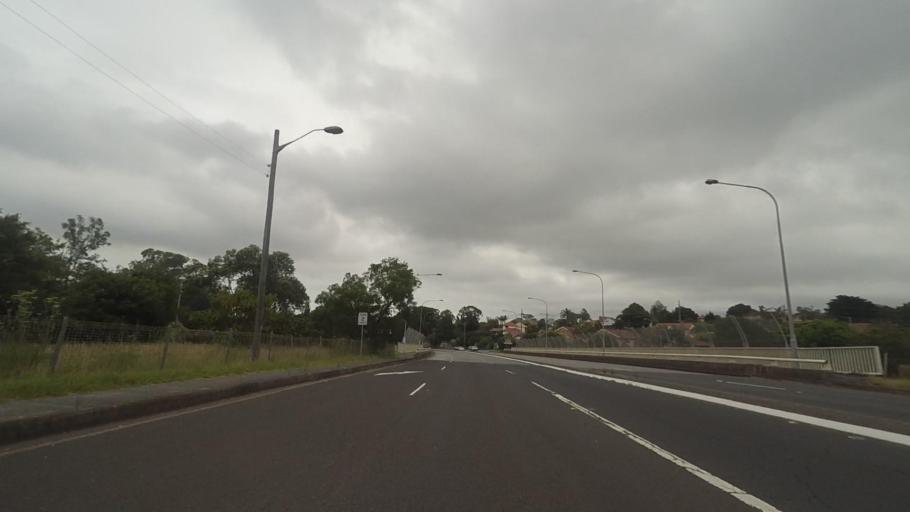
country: AU
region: New South Wales
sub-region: Wollongong
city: West Wollongong
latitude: -34.4286
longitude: 150.8676
